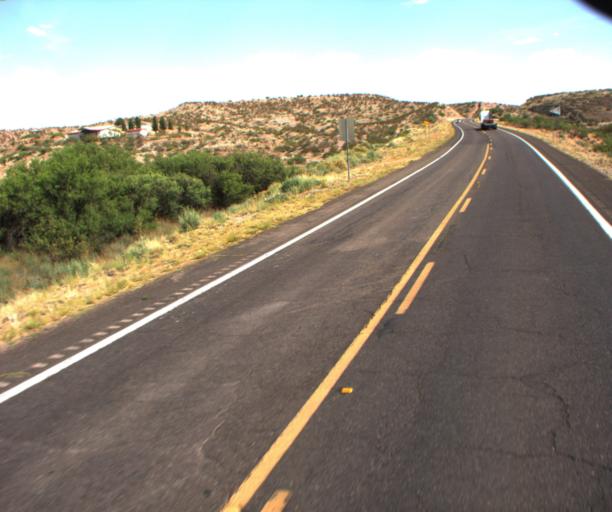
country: US
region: Arizona
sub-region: Greenlee County
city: Clifton
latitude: 32.9030
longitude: -109.1968
